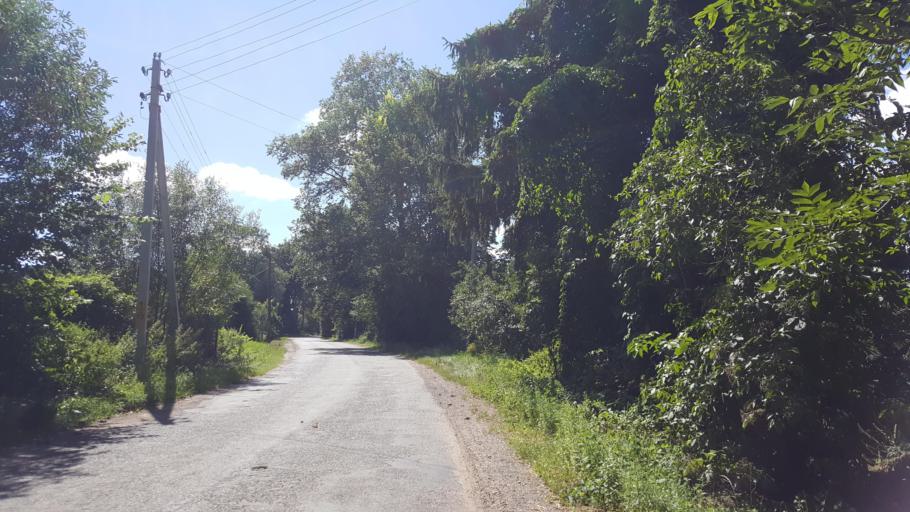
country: BY
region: Brest
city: Horad Kobryn
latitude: 52.2981
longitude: 24.3430
